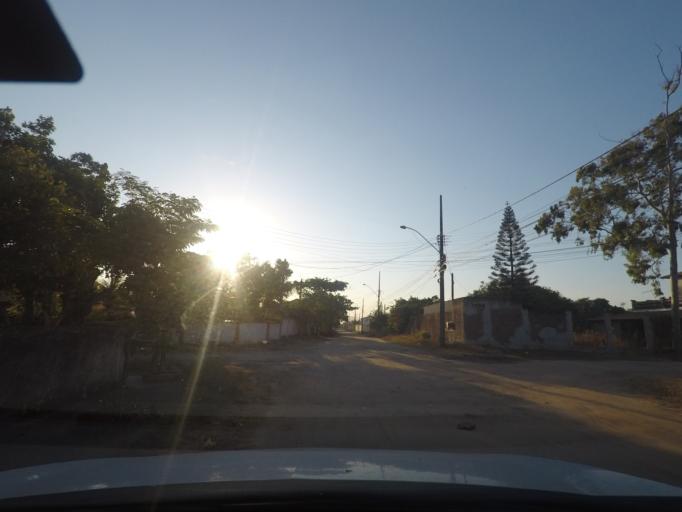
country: BR
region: Rio de Janeiro
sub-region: Marica
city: Marica
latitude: -22.9695
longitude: -42.9287
